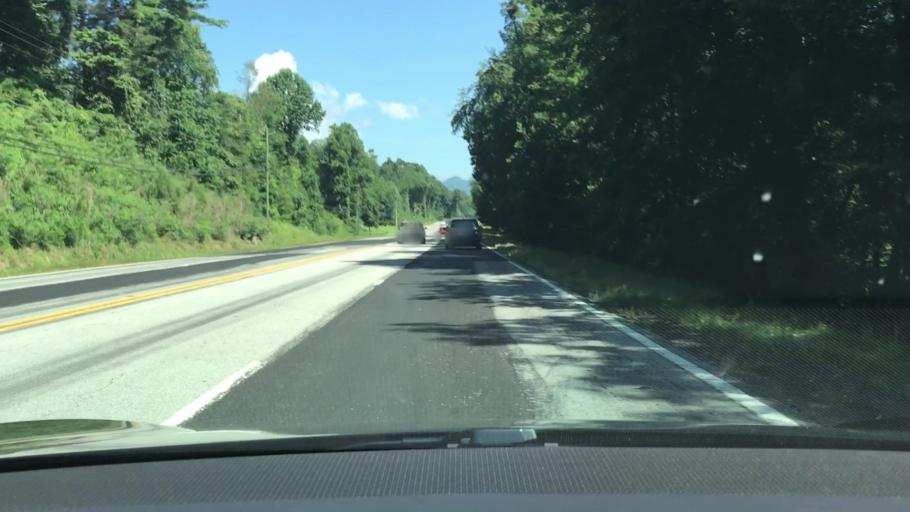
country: US
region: Georgia
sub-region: Rabun County
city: Mountain City
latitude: 34.9252
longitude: -83.3870
